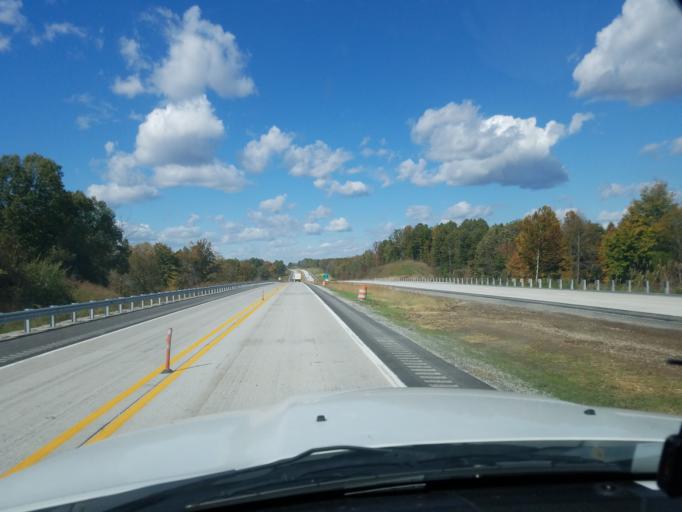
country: US
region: Kentucky
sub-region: Ohio County
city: Beaver Dam
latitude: 37.4357
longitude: -86.8522
